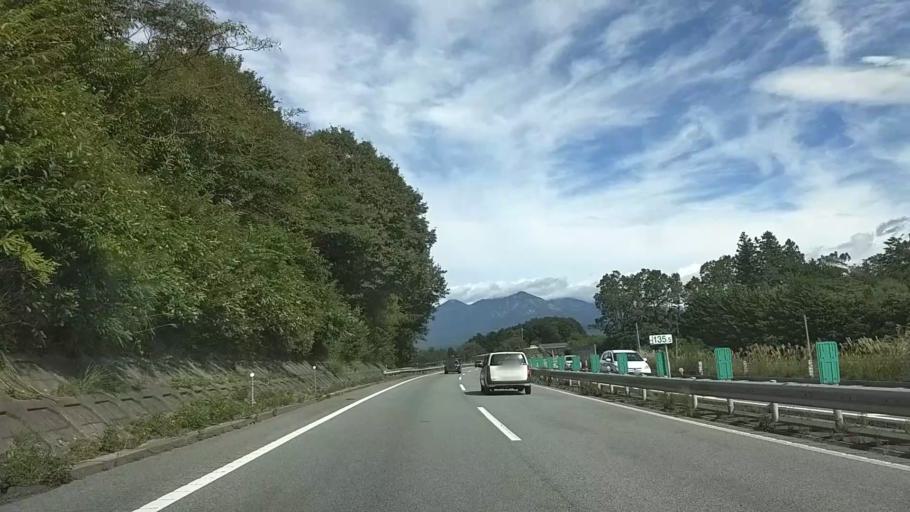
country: JP
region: Yamanashi
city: Nirasaki
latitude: 35.7967
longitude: 138.3959
